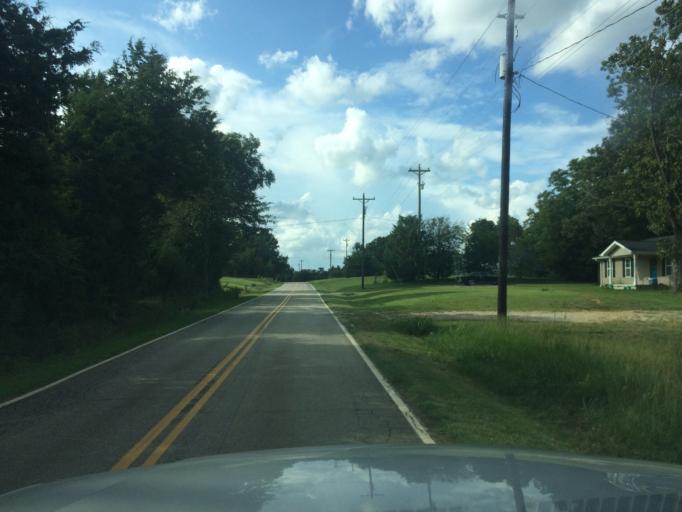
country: US
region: South Carolina
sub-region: Spartanburg County
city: Woodruff
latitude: 34.7639
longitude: -82.1032
